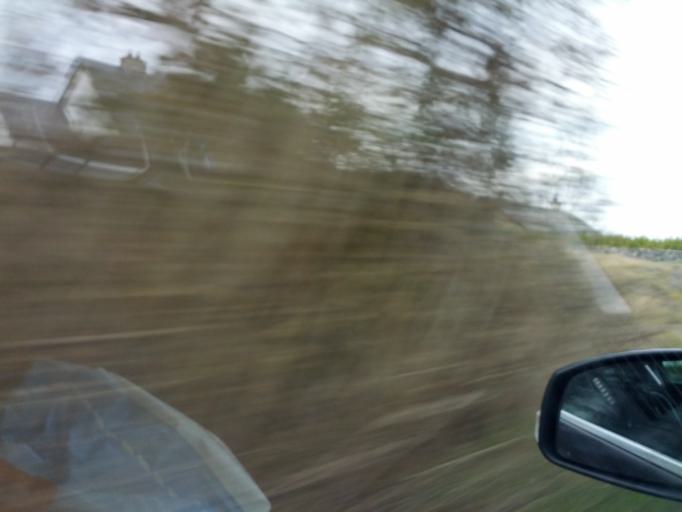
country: IE
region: Connaught
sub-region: County Galway
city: Athenry
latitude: 53.2641
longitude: -8.8250
